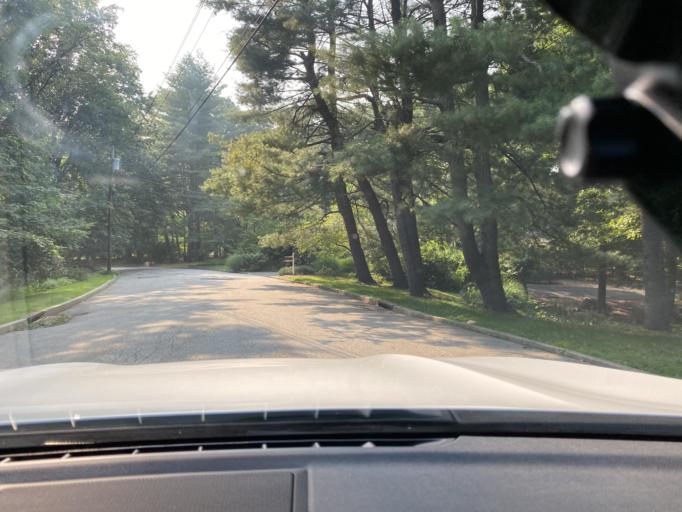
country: US
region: New Jersey
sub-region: Bergen County
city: Mahwah
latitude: 41.0977
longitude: -74.1376
